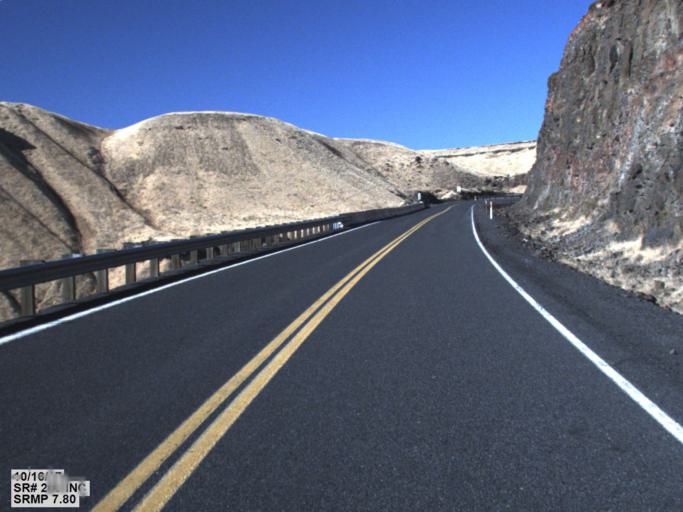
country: US
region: Washington
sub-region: Franklin County
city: Connell
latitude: 46.6260
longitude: -118.5606
